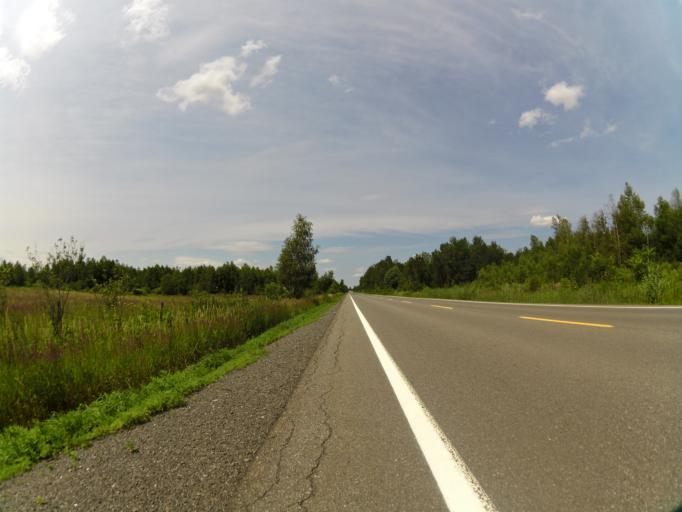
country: CA
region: Ontario
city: Ottawa
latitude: 45.2973
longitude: -75.6382
